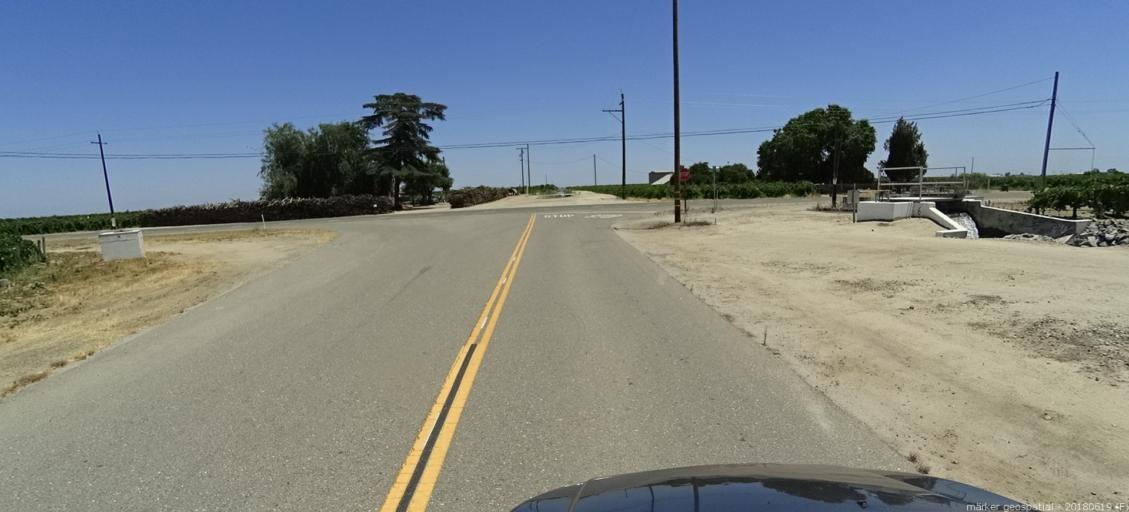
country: US
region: California
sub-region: Madera County
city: Parkwood
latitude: 36.8586
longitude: -120.0565
